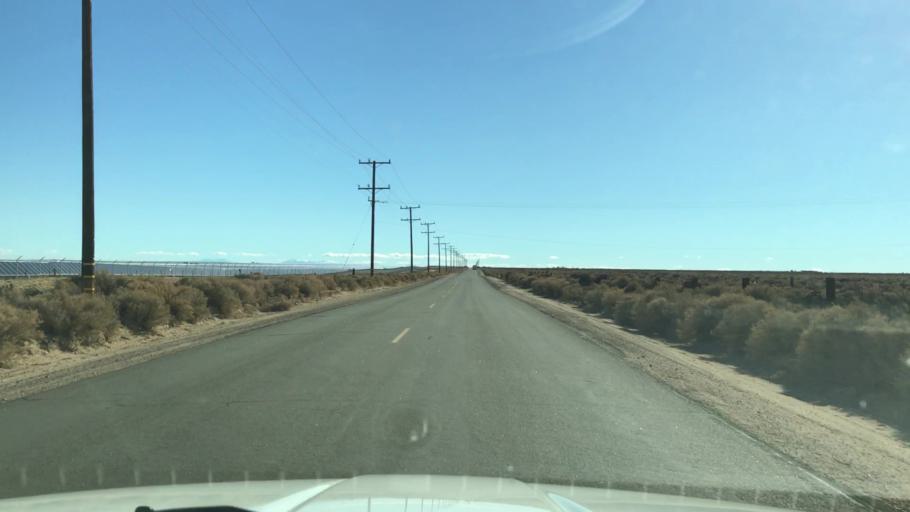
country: US
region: California
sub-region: Kern County
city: California City
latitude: 35.2541
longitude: -117.9860
